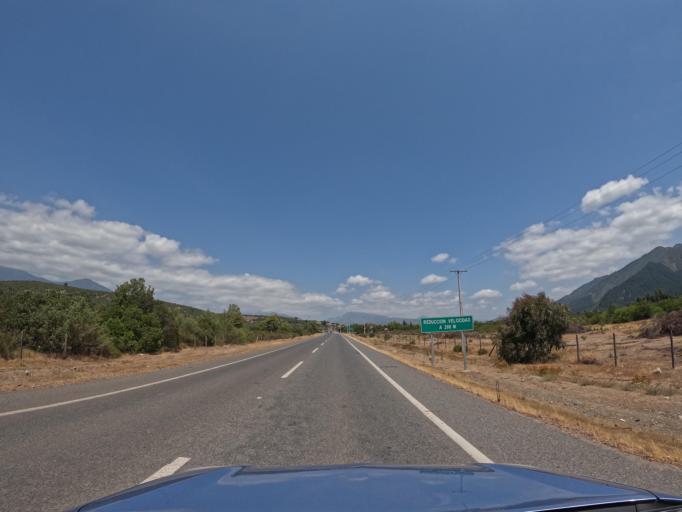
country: CL
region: Maule
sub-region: Provincia de Curico
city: Molina
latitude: -35.1743
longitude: -71.1240
